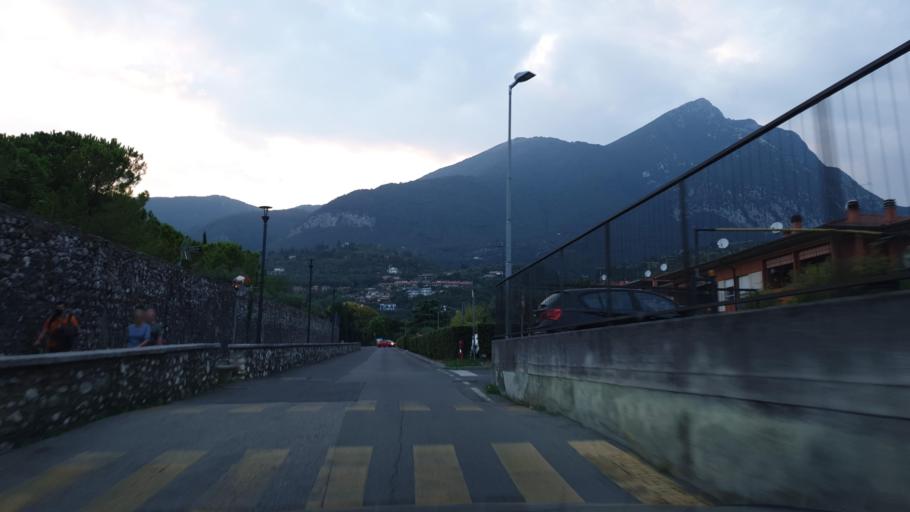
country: IT
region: Lombardy
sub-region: Provincia di Brescia
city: Toscolano Maderno
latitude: 45.6376
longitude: 10.6147
